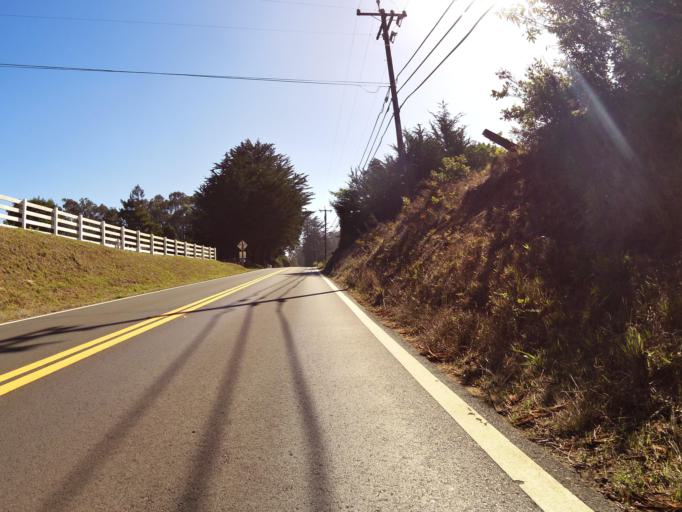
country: US
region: California
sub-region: Mendocino County
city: Fort Bragg
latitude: 39.5264
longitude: -123.7601
